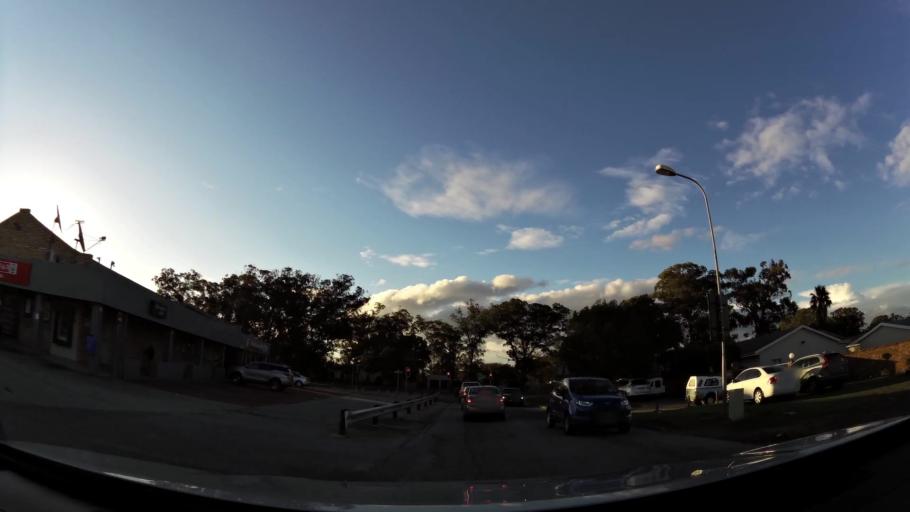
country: ZA
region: Eastern Cape
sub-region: Nelson Mandela Bay Metropolitan Municipality
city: Port Elizabeth
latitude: -33.9691
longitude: 25.4938
